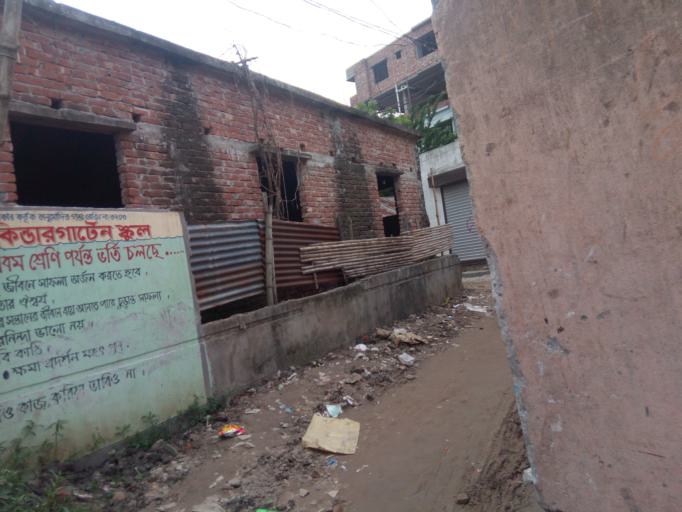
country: BD
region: Dhaka
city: Paltan
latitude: 23.7426
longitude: 90.4502
